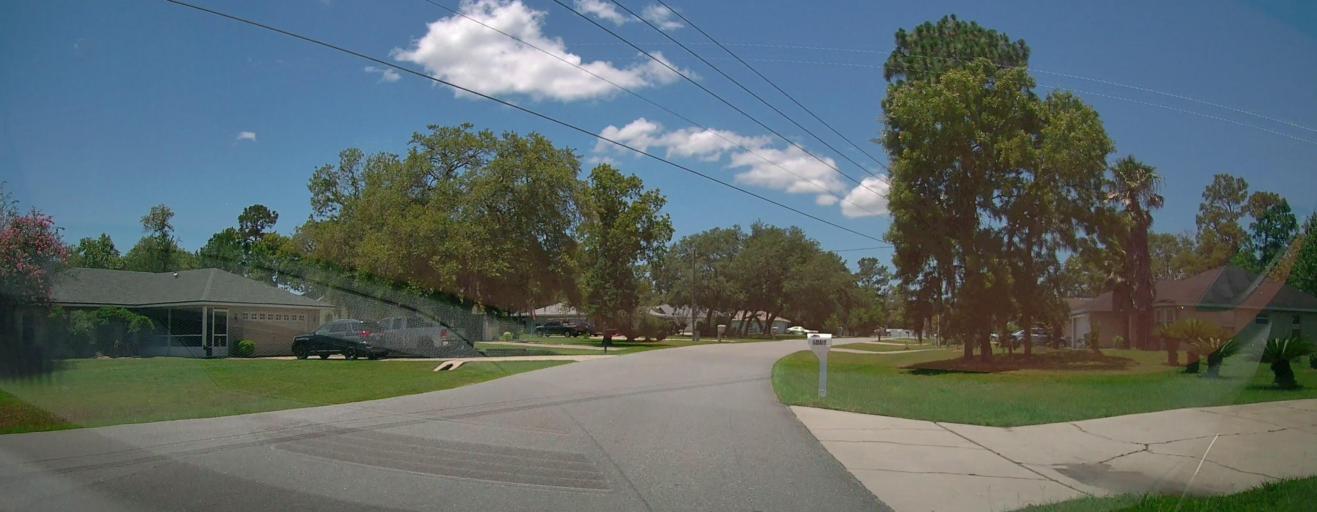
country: US
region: Florida
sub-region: Marion County
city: Silver Springs Shores
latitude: 29.1377
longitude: -82.0279
